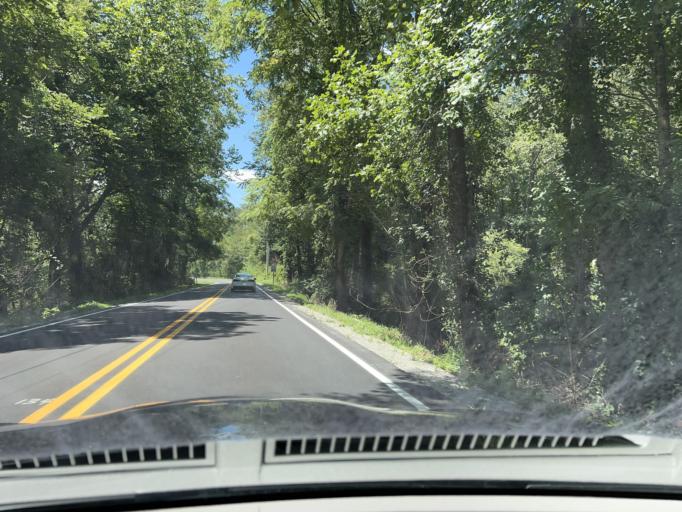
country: US
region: North Carolina
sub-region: Buncombe County
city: Fairview
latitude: 35.4937
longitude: -82.4296
